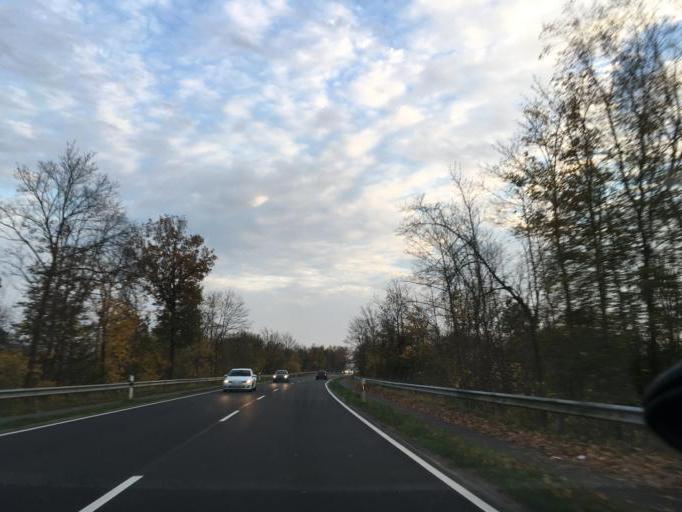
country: DE
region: Lower Saxony
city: Celle
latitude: 52.6428
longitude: 10.0766
